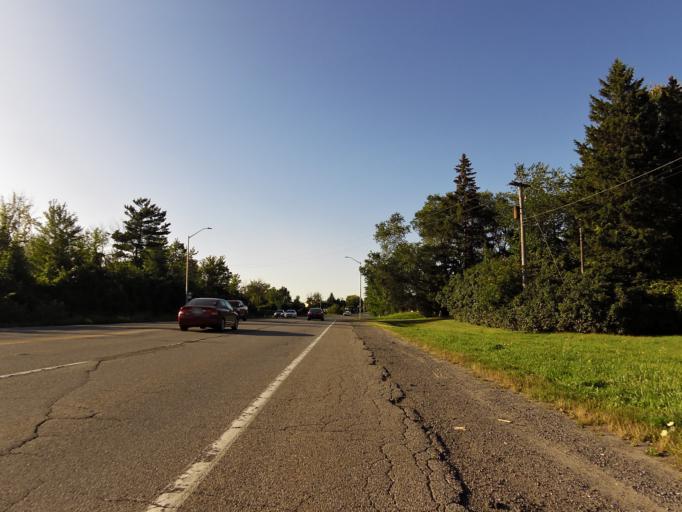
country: CA
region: Ontario
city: Ottawa
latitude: 45.3492
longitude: -75.7027
